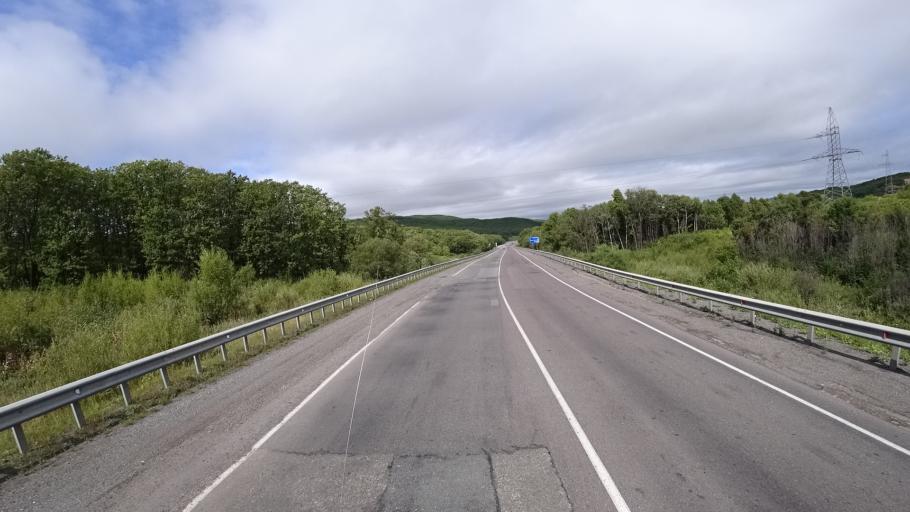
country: RU
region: Primorskiy
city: Lyalichi
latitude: 44.1337
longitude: 132.4273
